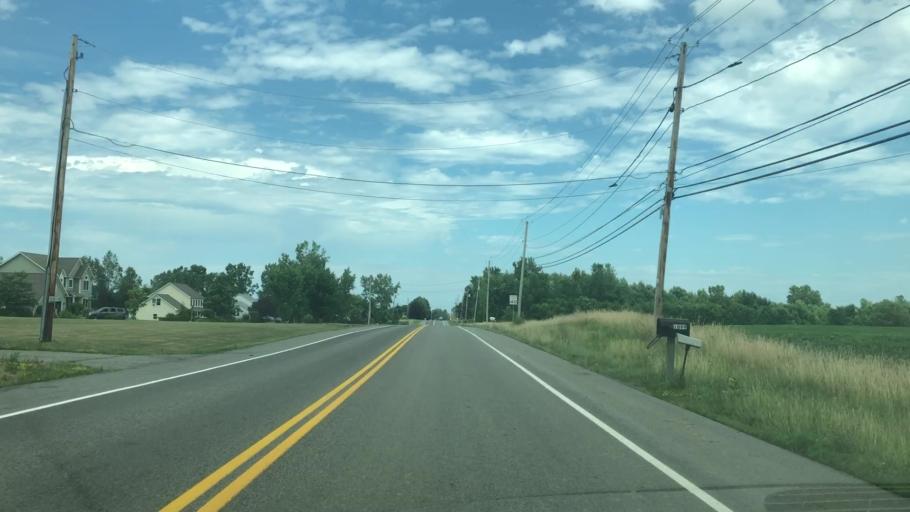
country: US
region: New York
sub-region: Monroe County
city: Webster
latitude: 43.1997
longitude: -77.4004
